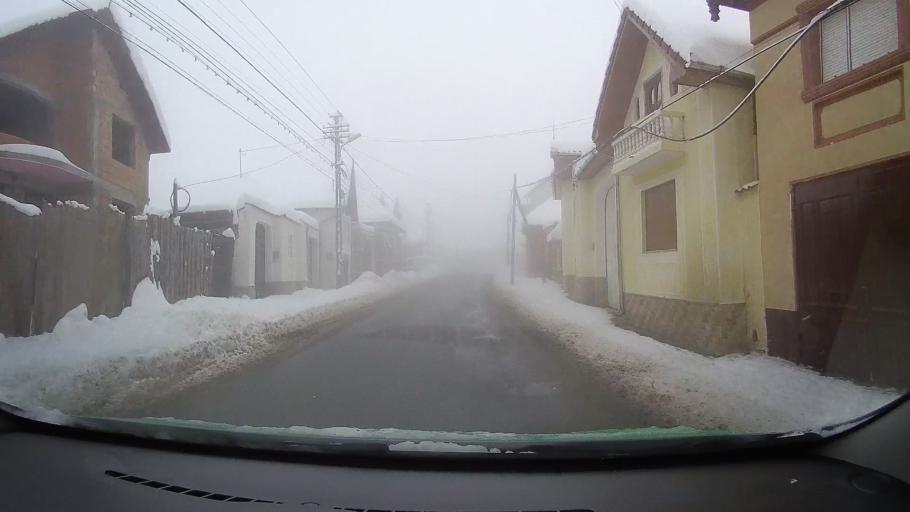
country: RO
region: Sibiu
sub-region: Comuna Jina
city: Jina
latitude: 45.7823
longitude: 23.6749
